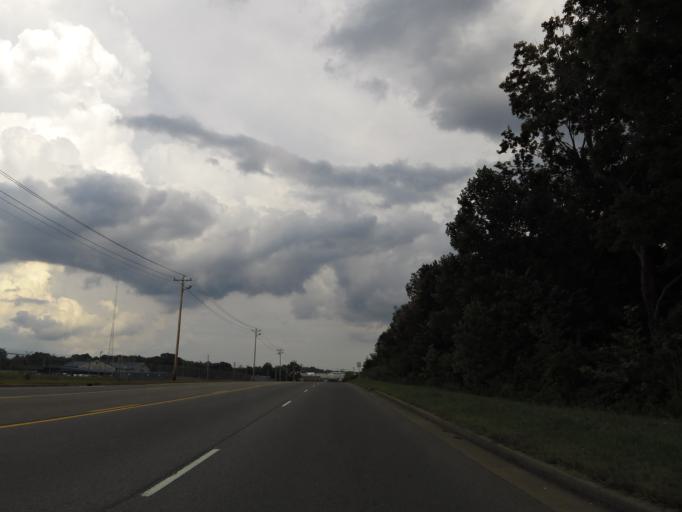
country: US
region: Tennessee
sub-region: Dickson County
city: Dickson
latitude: 36.0647
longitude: -87.3913
